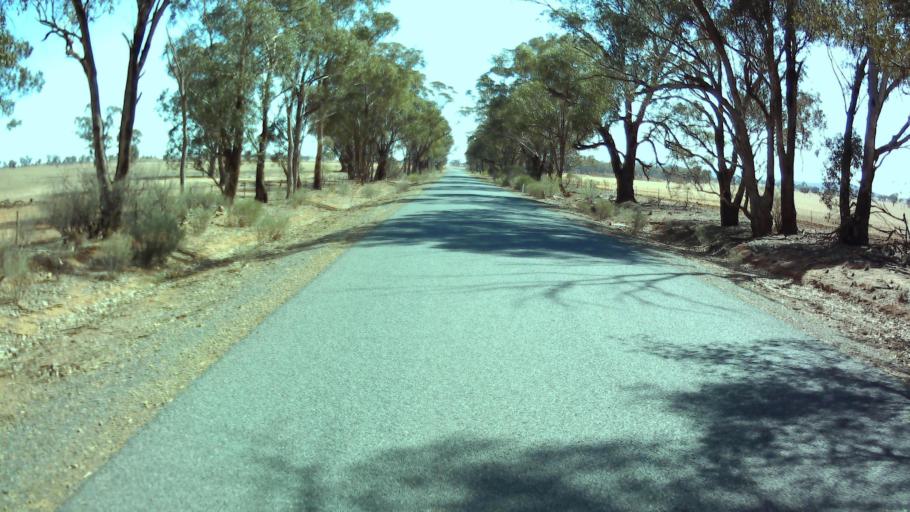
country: AU
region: New South Wales
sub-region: Weddin
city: Grenfell
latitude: -33.7406
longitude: 147.8814
